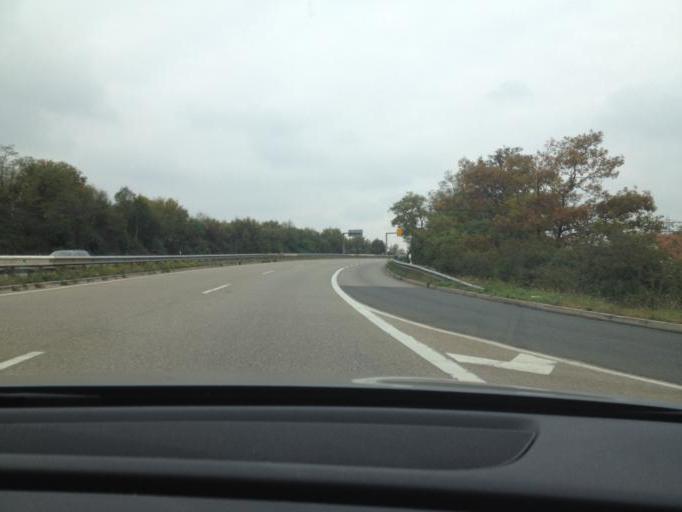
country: DE
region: Baden-Wuerttemberg
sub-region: Karlsruhe Region
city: Bruhl
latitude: 49.4193
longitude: 8.5378
